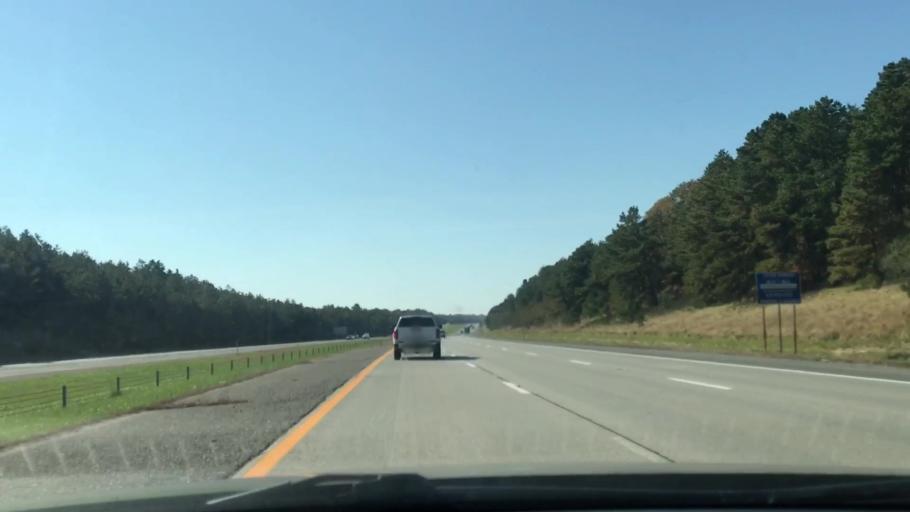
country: US
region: New York
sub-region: Suffolk County
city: Calverton
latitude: 40.8942
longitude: -72.7493
